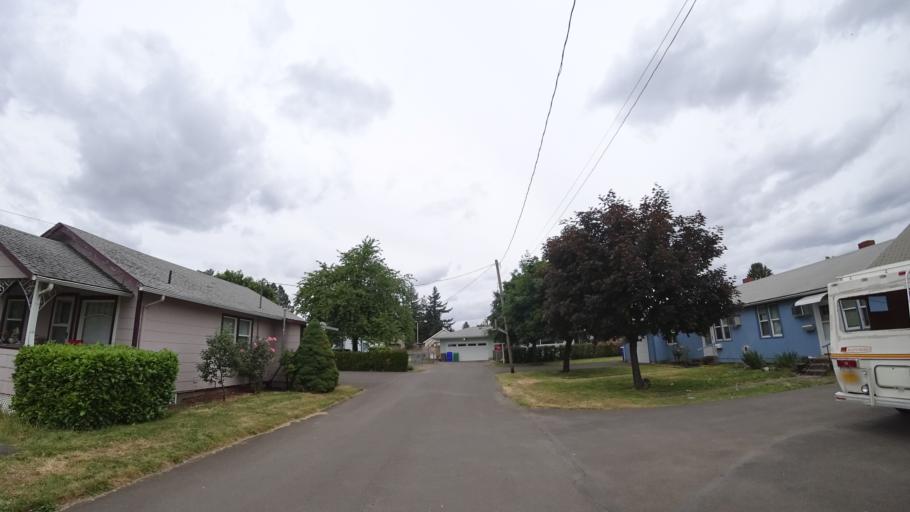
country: US
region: Oregon
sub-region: Multnomah County
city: Lents
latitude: 45.4670
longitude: -122.5839
